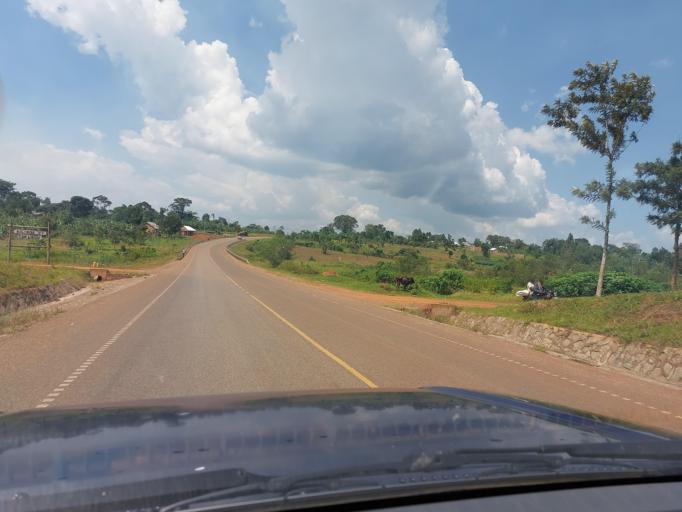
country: UG
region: Central Region
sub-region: Buikwe District
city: Buikwe
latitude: 0.3056
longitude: 33.0967
